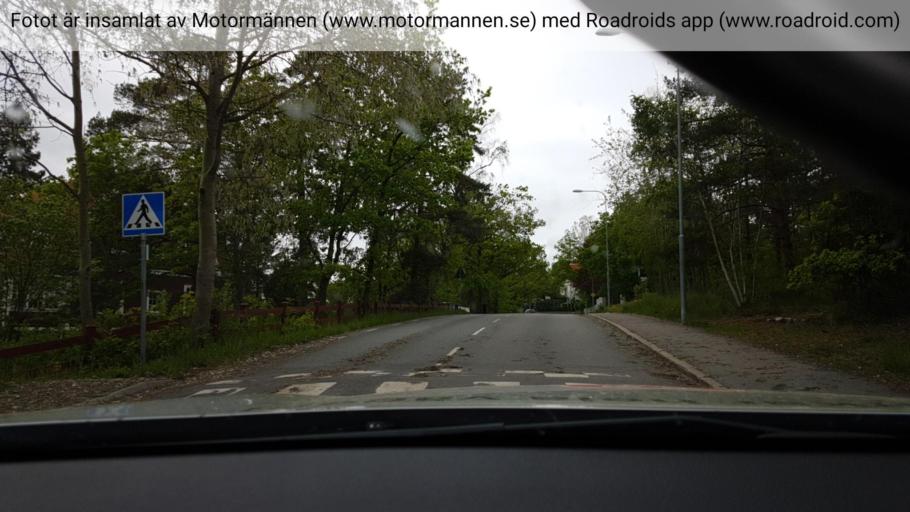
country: SE
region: Stockholm
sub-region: Lidingo
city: Brevik
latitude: 59.3468
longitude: 18.2181
